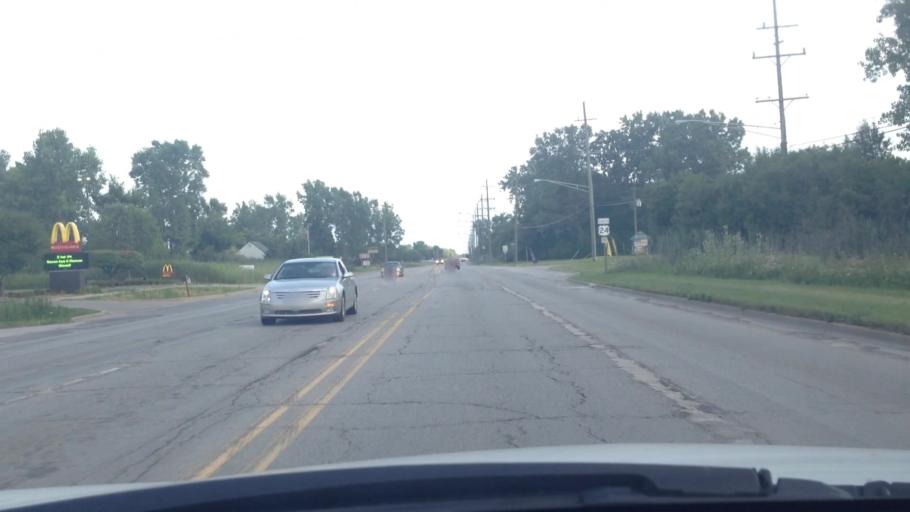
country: US
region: Michigan
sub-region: Wayne County
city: Woodhaven
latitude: 42.1669
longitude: -83.2668
